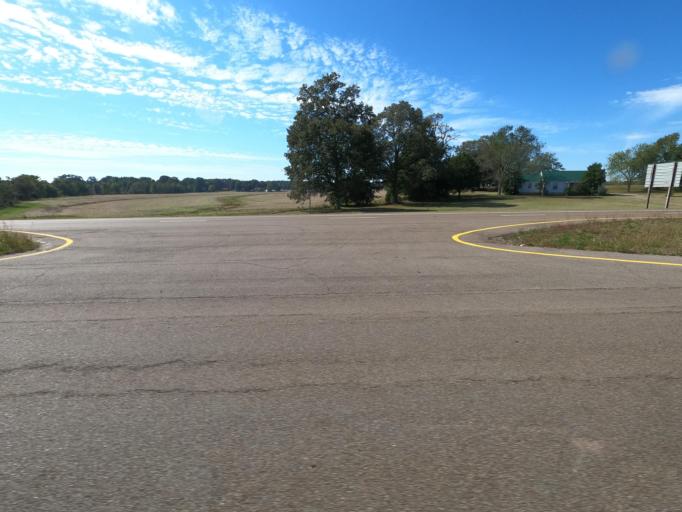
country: US
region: Tennessee
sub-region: Crockett County
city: Bells
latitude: 35.7210
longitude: -89.0596
